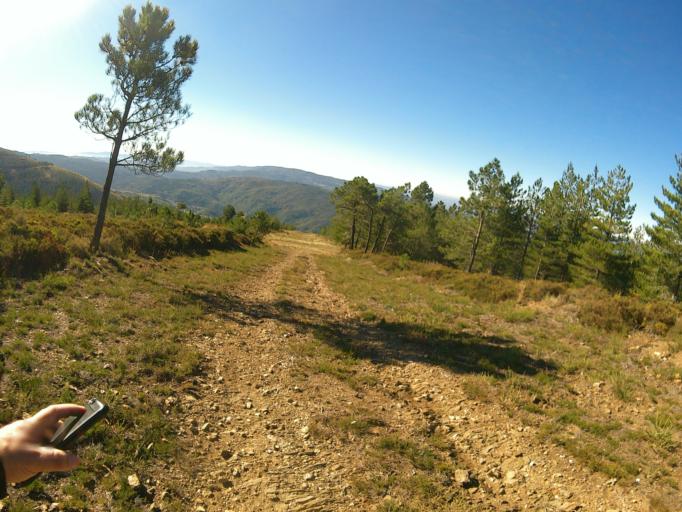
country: PT
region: Vila Real
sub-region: Mesao Frio
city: Mesao Frio
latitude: 41.2445
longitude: -7.9246
